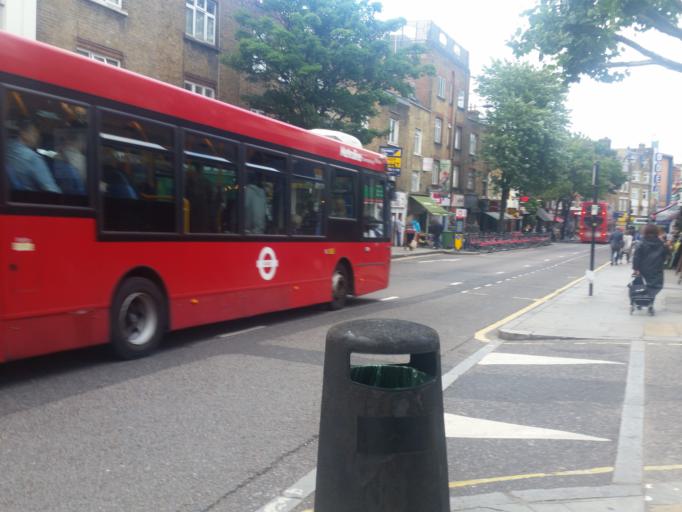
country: GB
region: England
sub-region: Greater London
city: Camden Town
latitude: 51.5378
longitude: -0.1446
